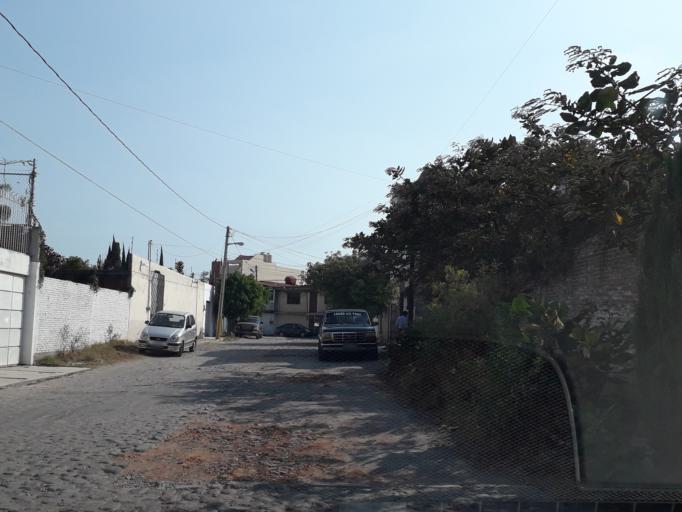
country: MX
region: Puebla
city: Puebla
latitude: 19.0139
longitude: -98.2105
